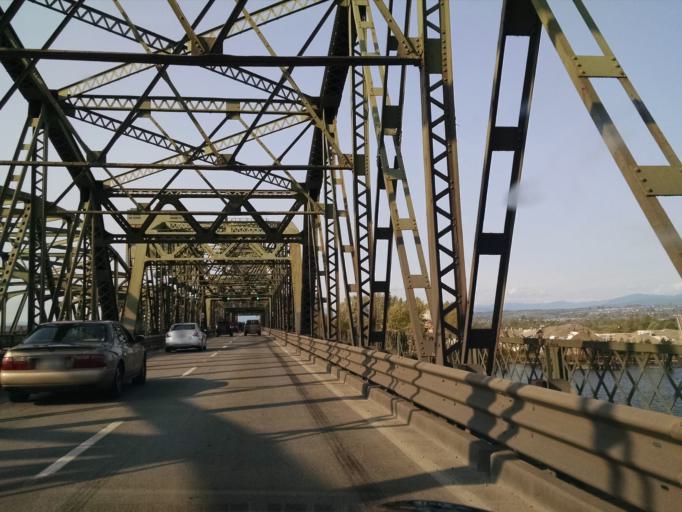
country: US
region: Washington
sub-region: Snohomish County
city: Marysville
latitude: 48.0156
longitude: -122.1878
